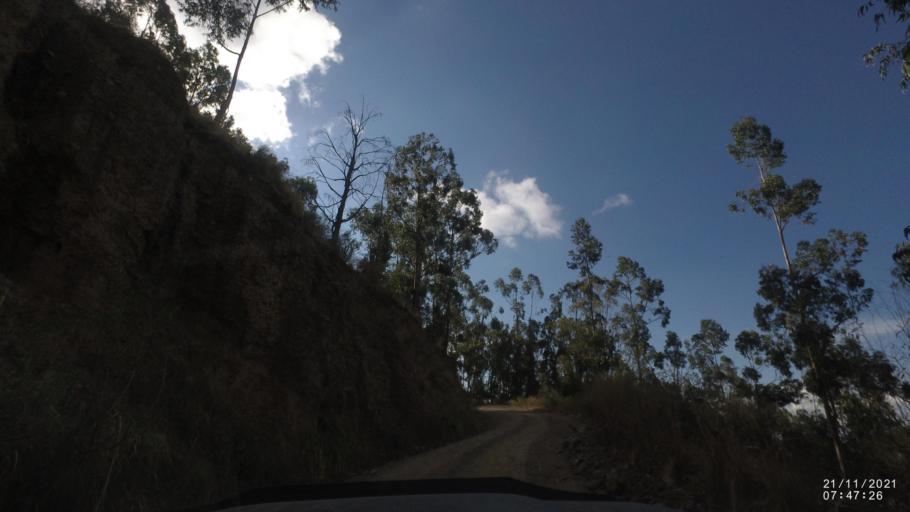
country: BO
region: Cochabamba
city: Cochabamba
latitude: -17.3095
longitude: -66.2191
